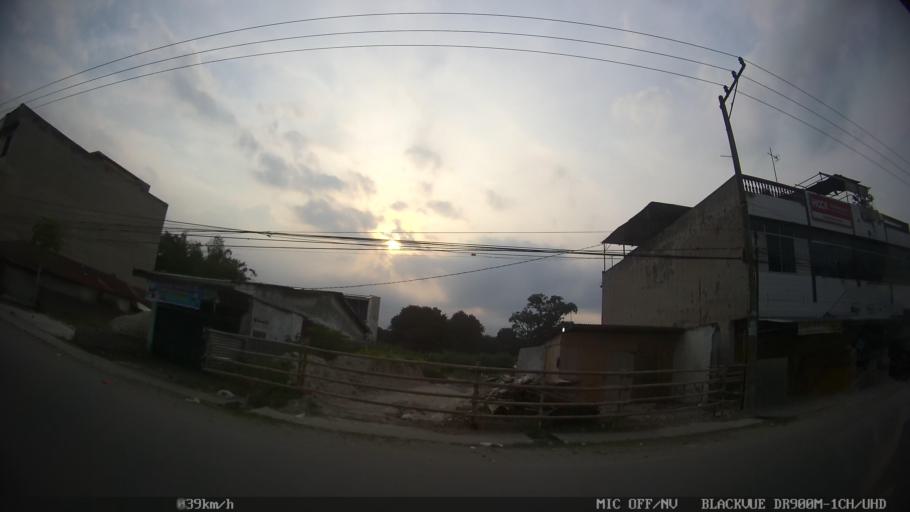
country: ID
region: North Sumatra
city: Sunggal
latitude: 3.5923
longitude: 98.6089
